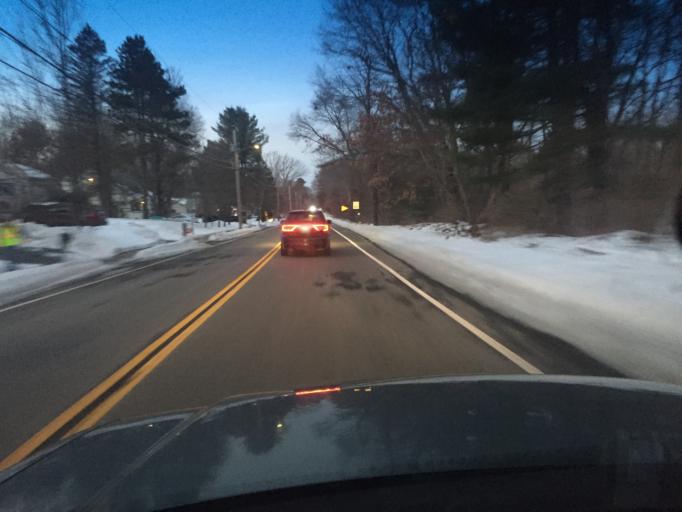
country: US
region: Massachusetts
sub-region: Norfolk County
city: Medway
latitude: 42.1209
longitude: -71.4293
